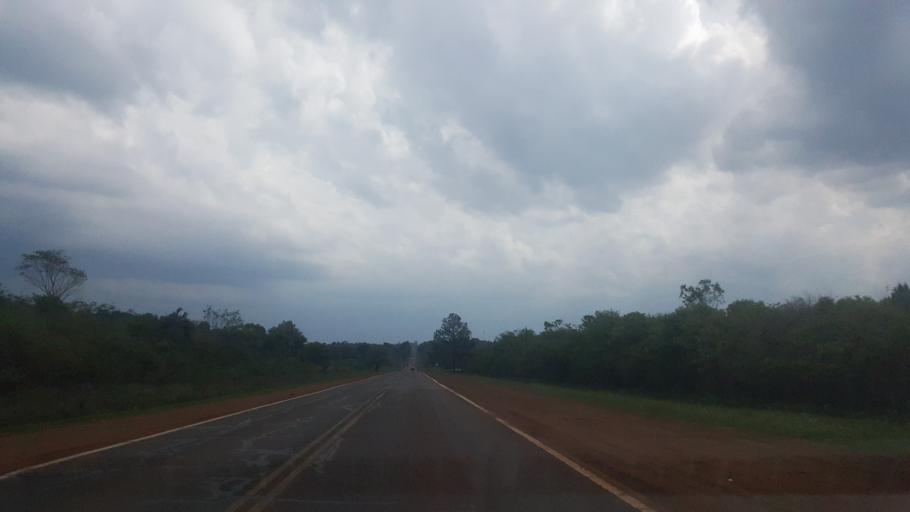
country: AR
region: Misiones
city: Santo Pipo
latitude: -27.1174
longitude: -55.3672
